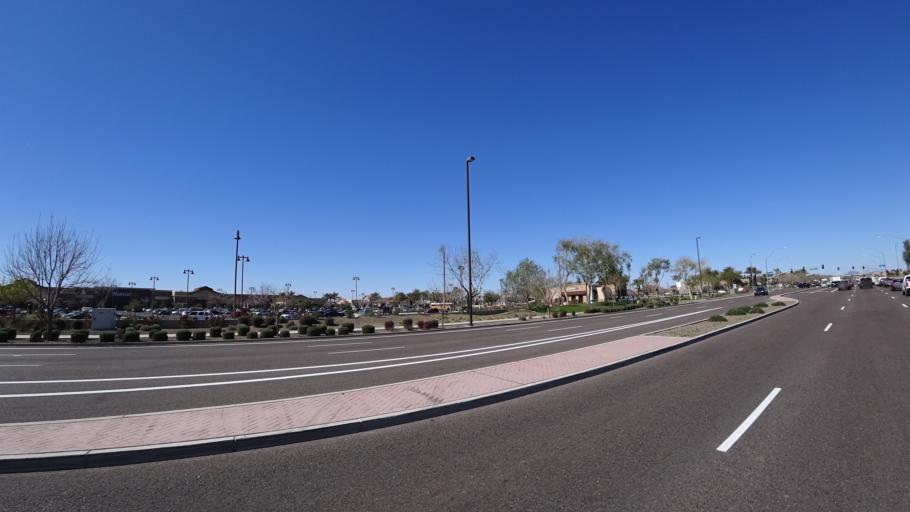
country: US
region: Arizona
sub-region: Maricopa County
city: Queen Creek
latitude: 33.3200
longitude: -111.6868
